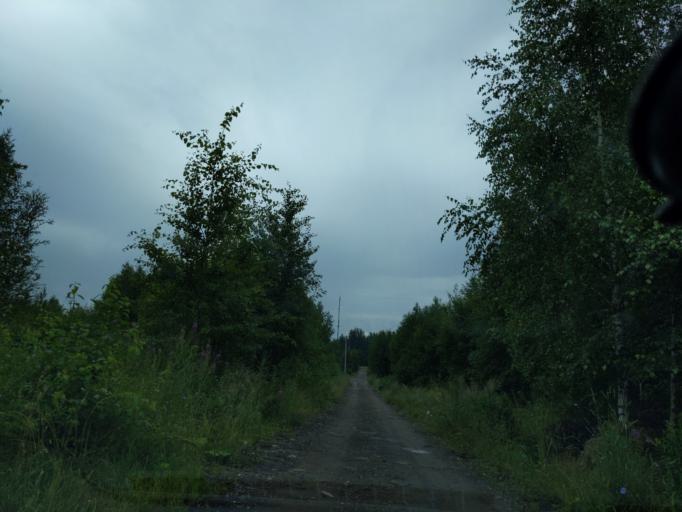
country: RU
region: Moskovskaya
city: Lugovaya
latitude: 56.0555
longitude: 37.4979
